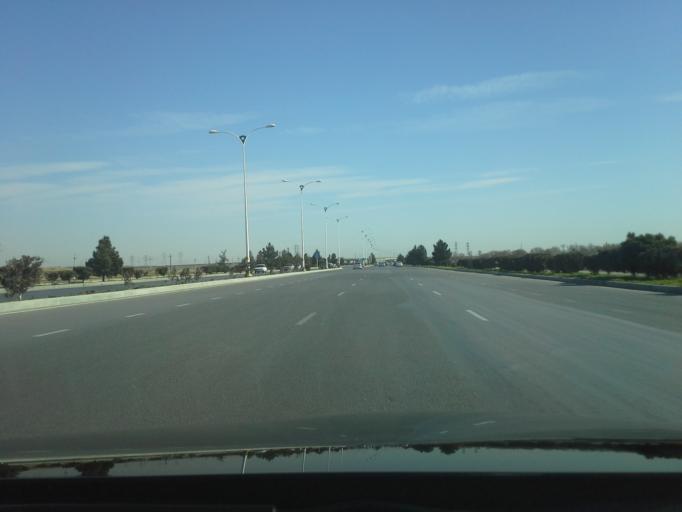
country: TM
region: Ahal
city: Annau
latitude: 37.9160
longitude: 58.4716
